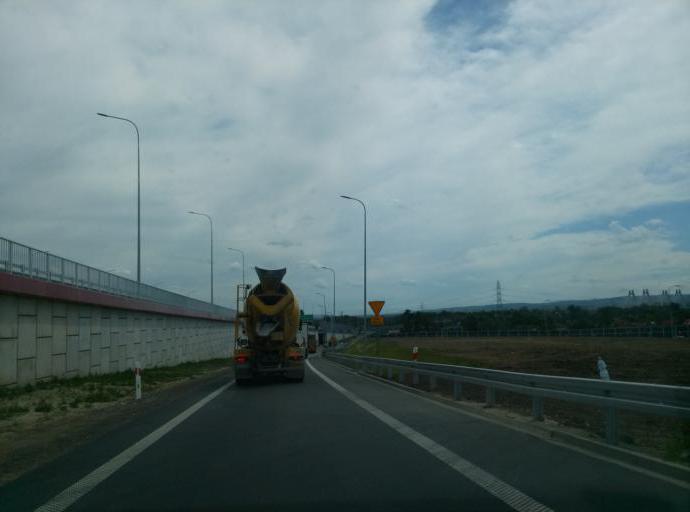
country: PL
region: Lesser Poland Voivodeship
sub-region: Powiat wielicki
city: Kokotow
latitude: 50.0657
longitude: 20.0711
